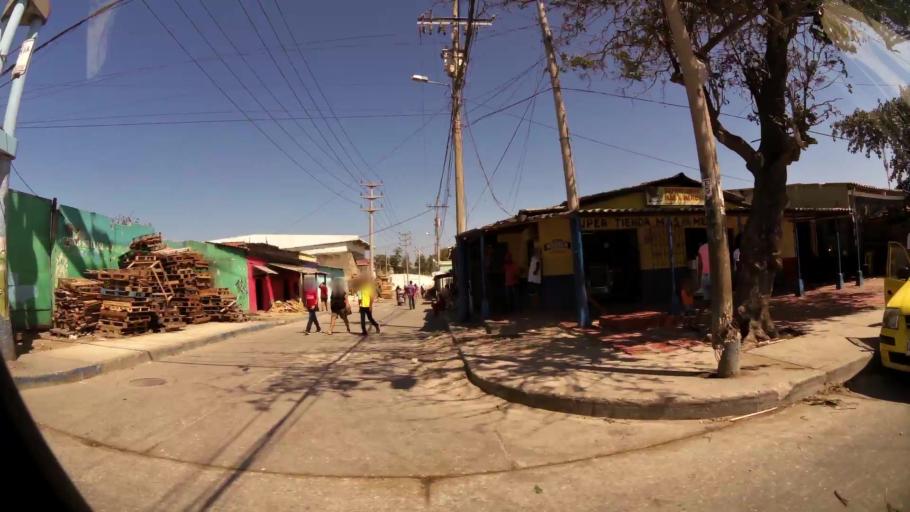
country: CO
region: Atlantico
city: Barranquilla
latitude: 10.9740
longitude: -74.7750
